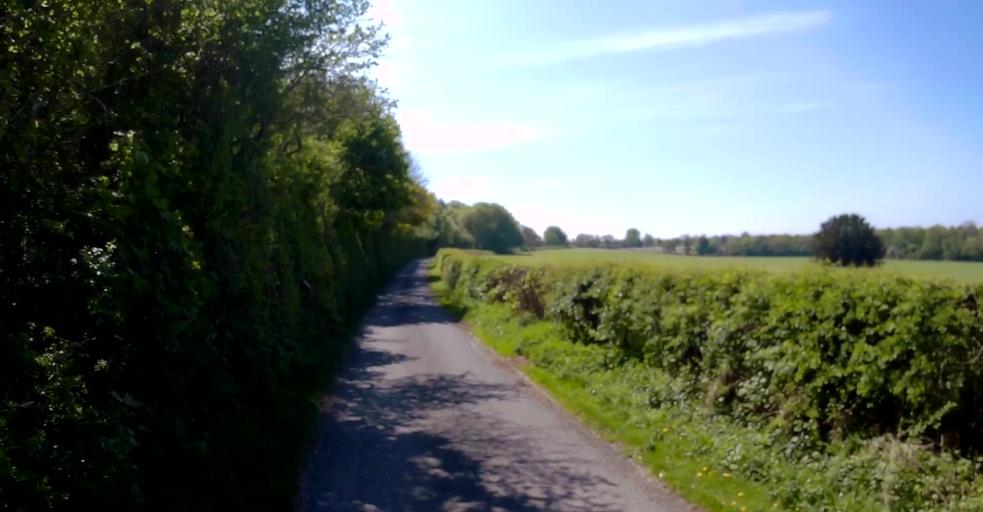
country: GB
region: England
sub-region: Hampshire
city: Overton
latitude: 51.1988
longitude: -1.2430
